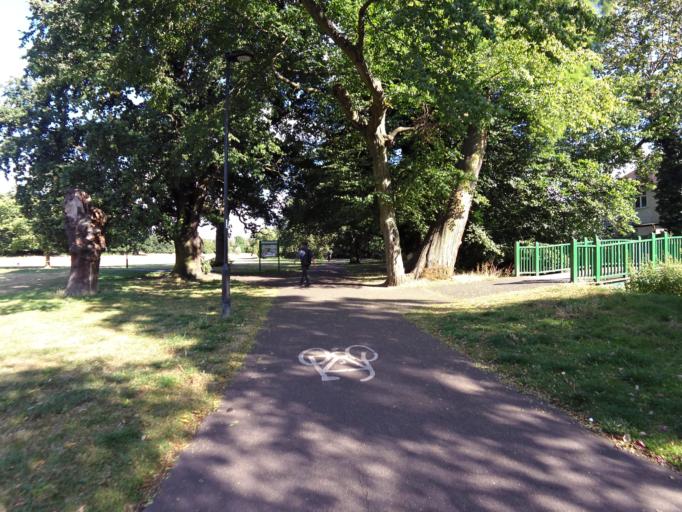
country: GB
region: England
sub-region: Greater London
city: Wood Green
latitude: 51.6181
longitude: -0.1314
